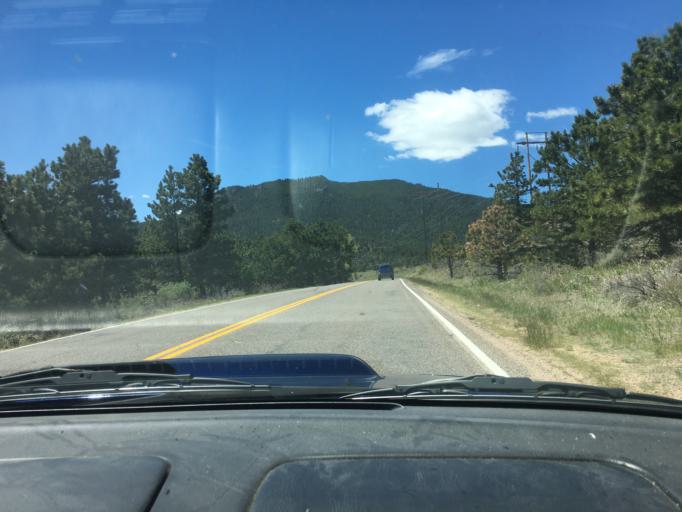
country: US
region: Colorado
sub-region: Larimer County
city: Estes Park
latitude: 40.3519
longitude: -105.5275
